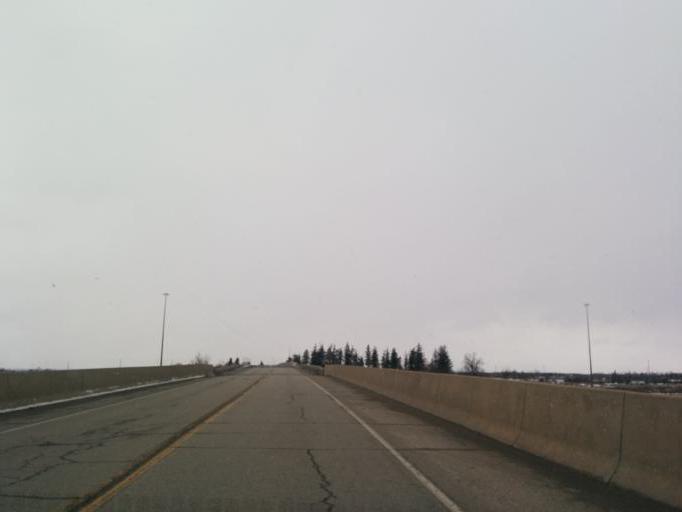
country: CA
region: Ontario
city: Brampton
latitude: 43.5900
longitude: -79.8080
